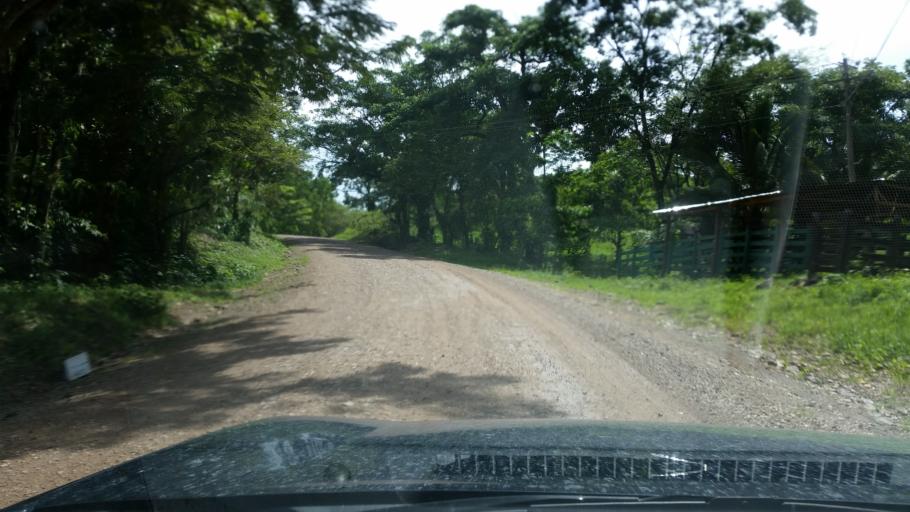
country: NI
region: Atlantico Norte (RAAN)
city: Siuna
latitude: 13.6813
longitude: -84.6513
